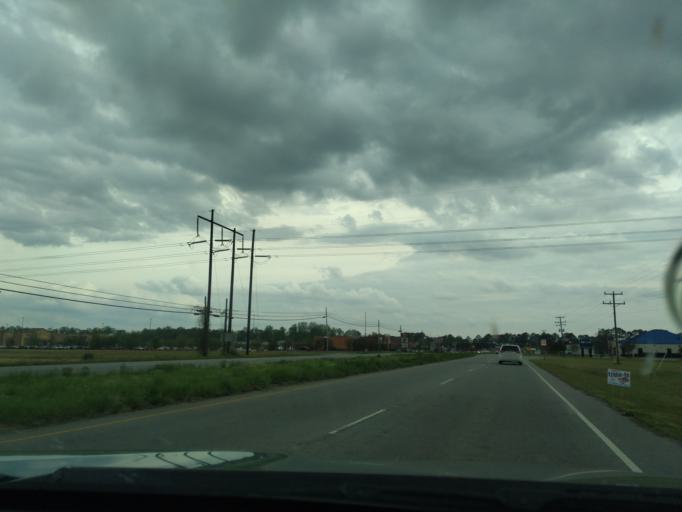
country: US
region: North Carolina
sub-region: Martin County
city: Williamston
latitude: 35.8373
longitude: -77.0655
